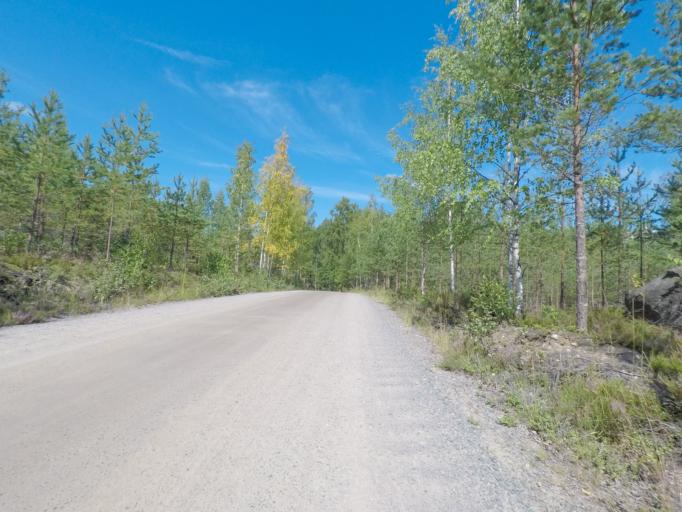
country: FI
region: Southern Savonia
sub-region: Mikkeli
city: Puumala
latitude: 61.4131
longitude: 28.0476
